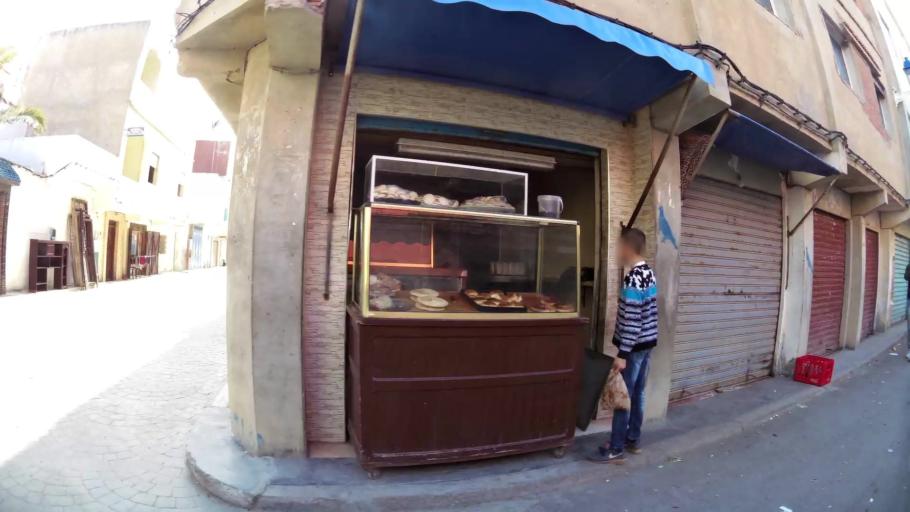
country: MA
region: Tanger-Tetouan
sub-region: Tetouan
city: Martil
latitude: 35.6104
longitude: -5.2726
